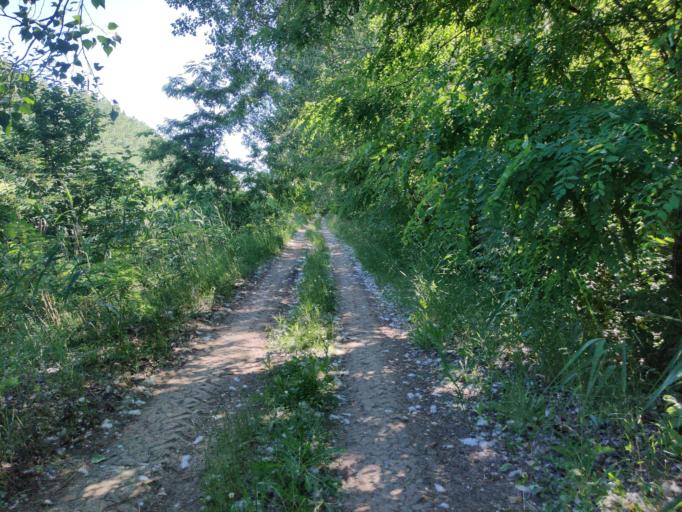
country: HU
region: Hajdu-Bihar
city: Balmazujvaros
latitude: 47.5842
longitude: 21.3555
